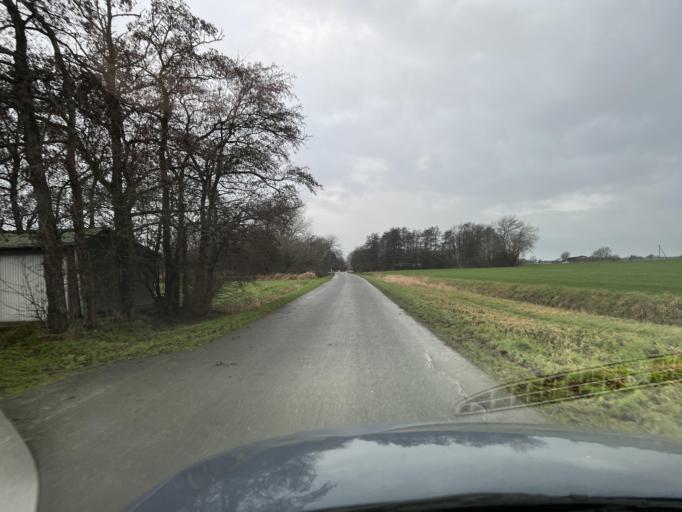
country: DE
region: Schleswig-Holstein
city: Hillgroven
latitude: 54.2172
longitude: 8.8789
